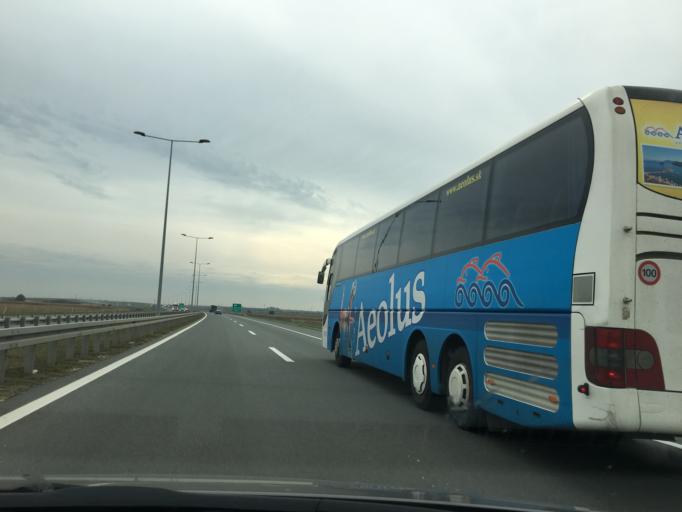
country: RS
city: Dobanovci
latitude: 44.8585
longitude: 20.2501
